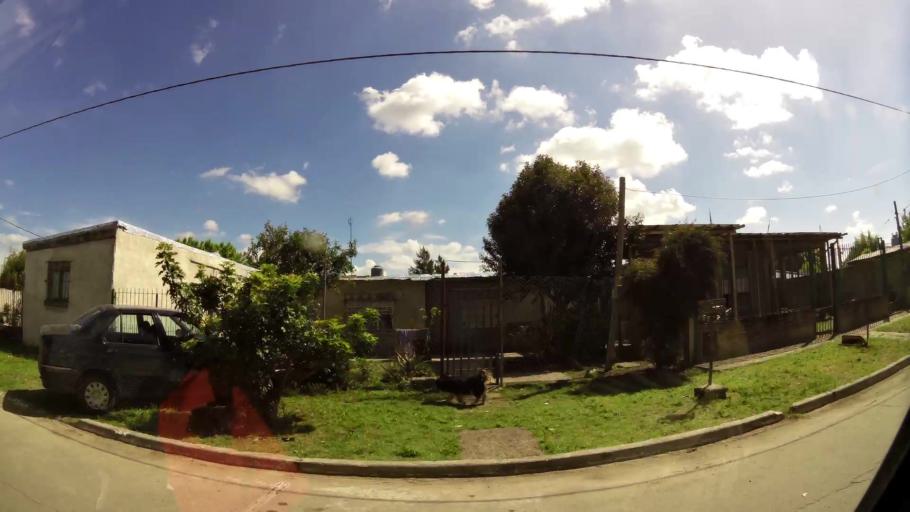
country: AR
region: Buenos Aires
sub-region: Partido de Quilmes
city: Quilmes
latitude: -34.8214
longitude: -58.2629
